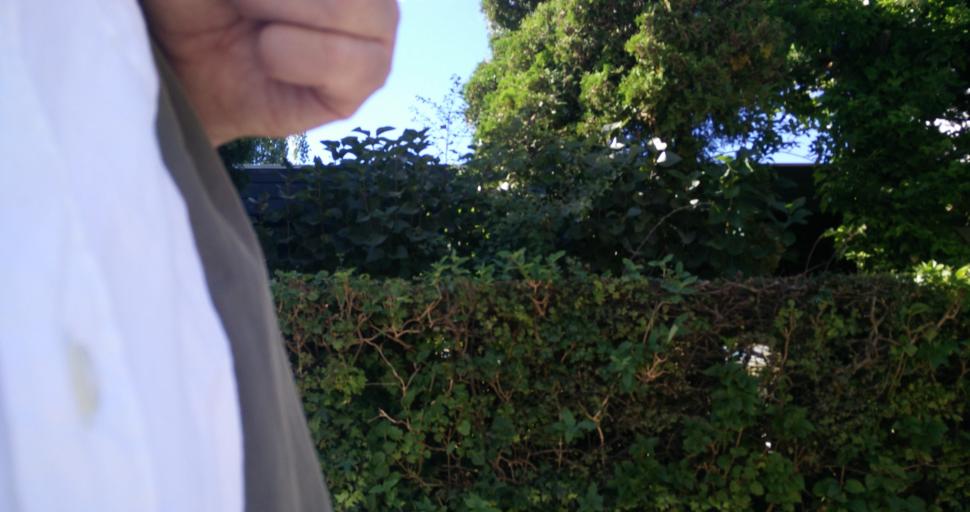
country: DK
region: Capital Region
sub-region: Lyngby-Tarbaek Kommune
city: Kongens Lyngby
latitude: 55.7678
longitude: 12.5100
